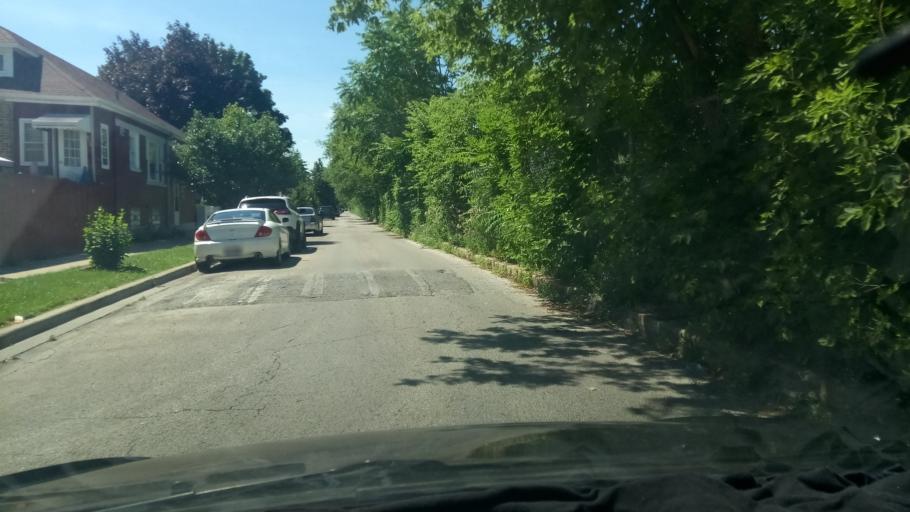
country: US
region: Illinois
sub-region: Cook County
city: Hometown
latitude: 41.7771
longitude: -87.7126
